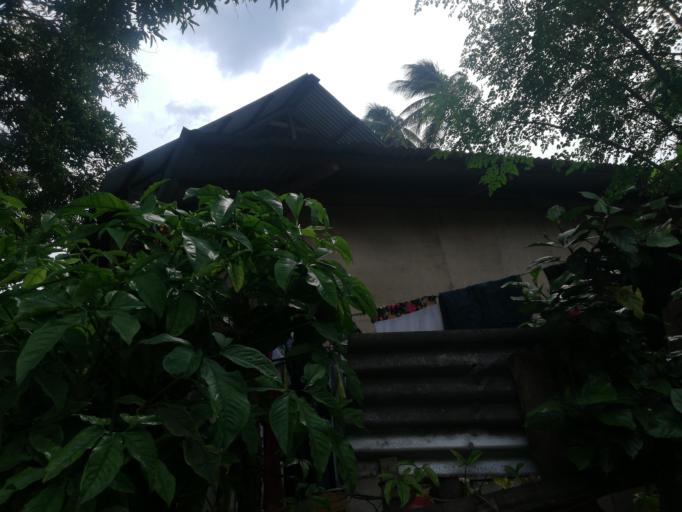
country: PH
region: Central Visayas
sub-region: Province of Negros Oriental
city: Dumaguete
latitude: 9.3034
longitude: 123.3001
